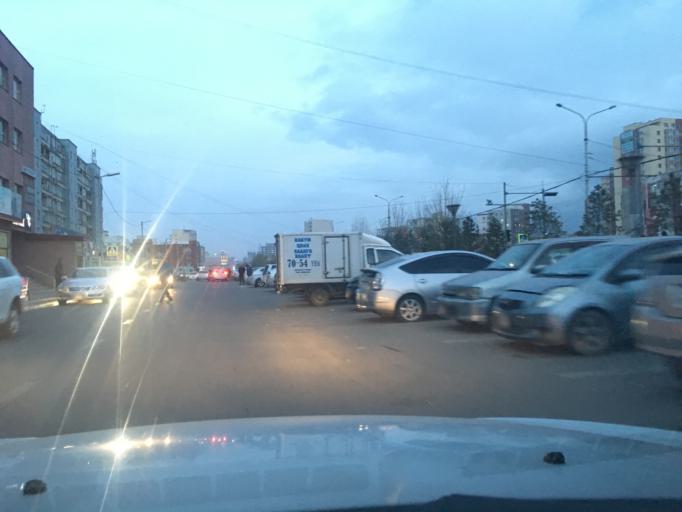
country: MN
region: Ulaanbaatar
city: Ulaanbaatar
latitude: 47.9141
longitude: 106.8668
